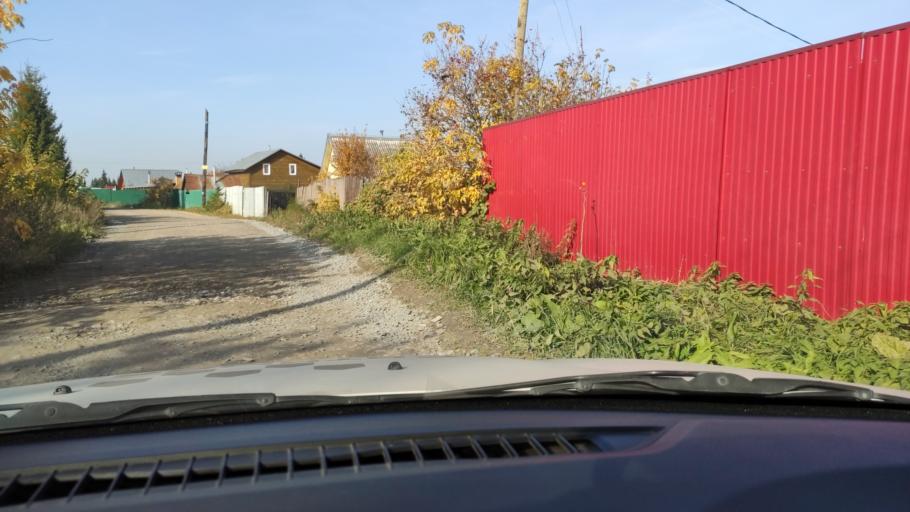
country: RU
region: Perm
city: Sylva
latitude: 58.0446
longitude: 56.7460
